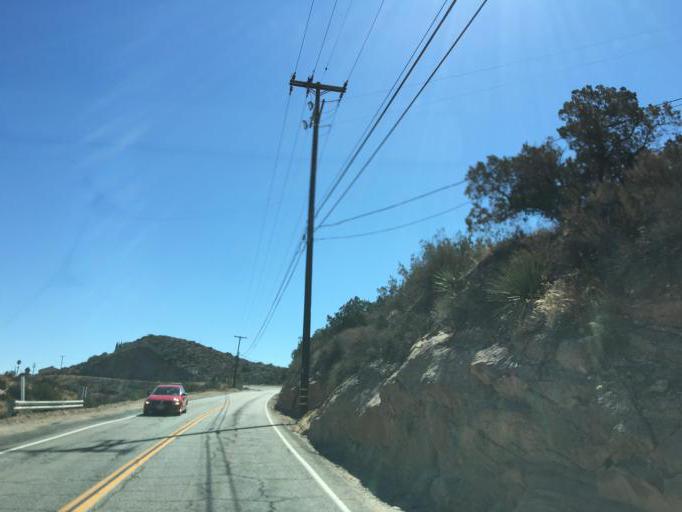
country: US
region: California
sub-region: Los Angeles County
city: Agua Dulce
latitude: 34.4769
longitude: -118.3529
